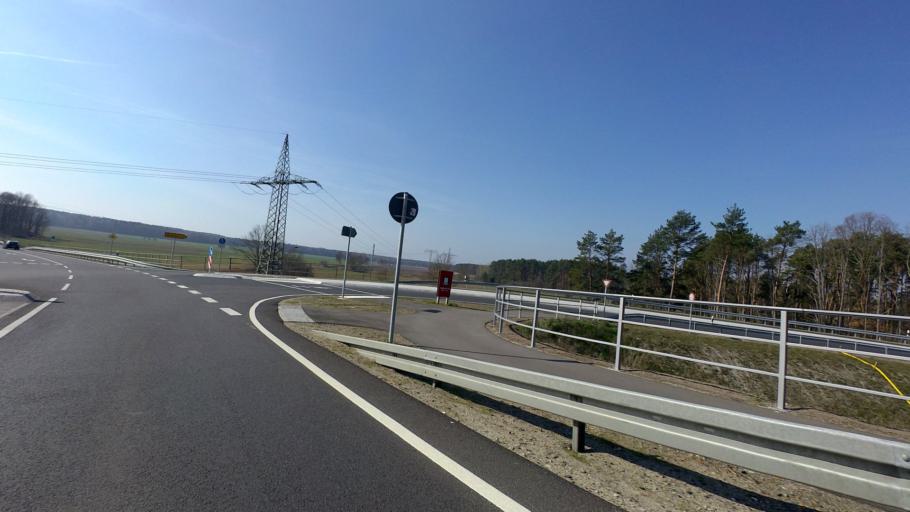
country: DE
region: Brandenburg
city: Zossen
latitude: 52.1353
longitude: 13.4782
